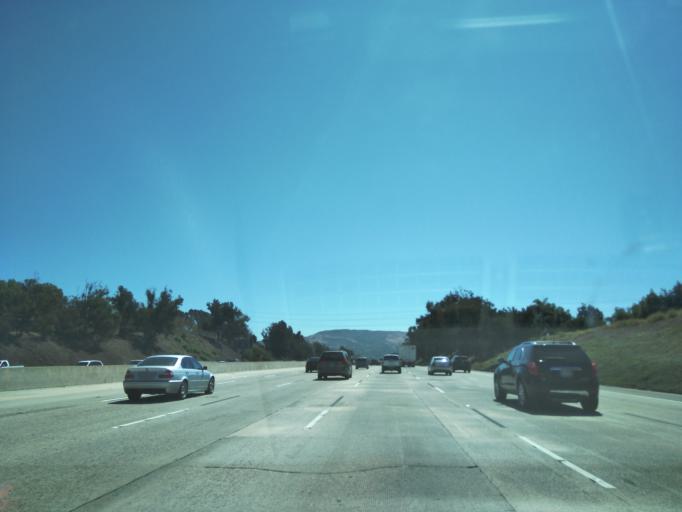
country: US
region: California
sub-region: Orange County
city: San Juan Capistrano
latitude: 33.5150
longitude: -117.6636
